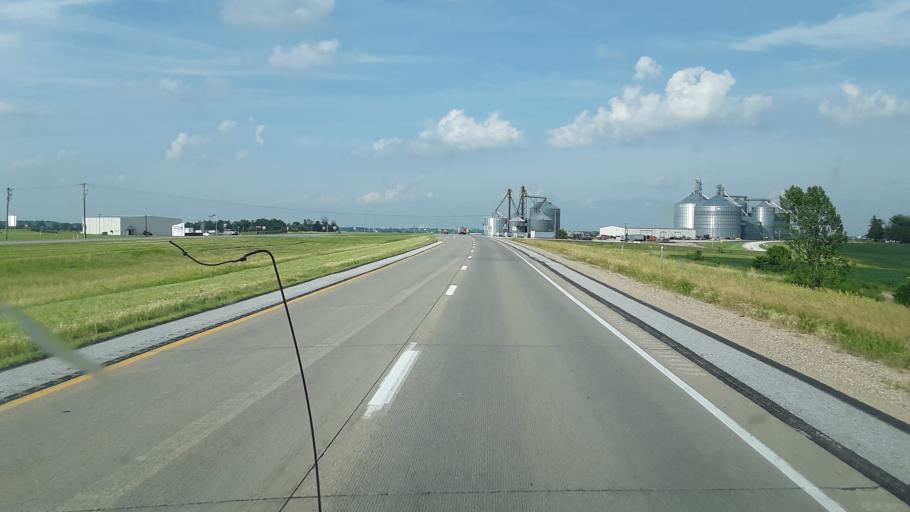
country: US
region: Iowa
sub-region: Marshall County
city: Marshalltown
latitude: 42.0032
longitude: -93.0264
